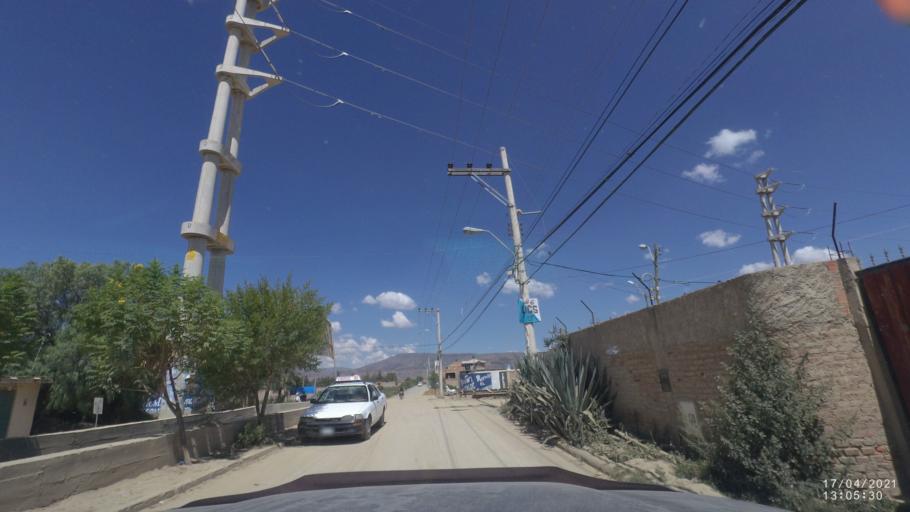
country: BO
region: Cochabamba
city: Cochabamba
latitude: -17.4057
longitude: -66.2251
